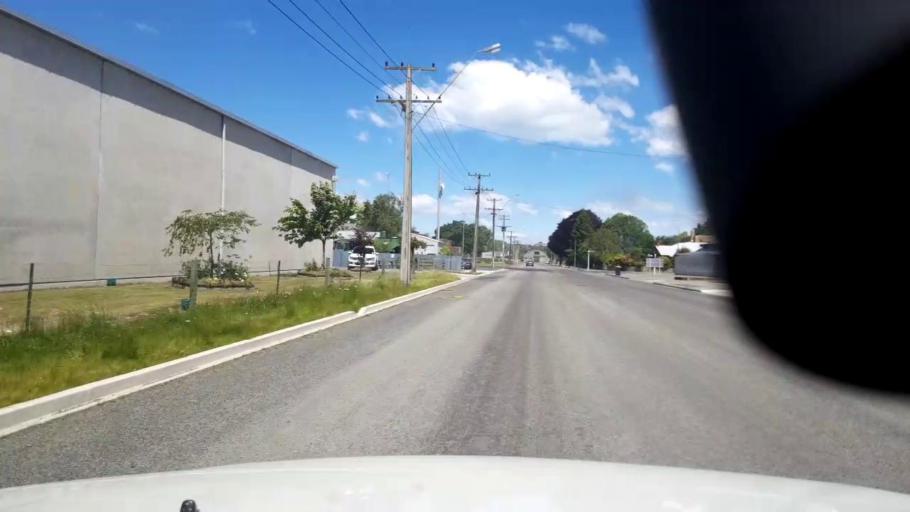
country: NZ
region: Canterbury
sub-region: Timaru District
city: Pleasant Point
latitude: -44.2404
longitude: 171.2792
